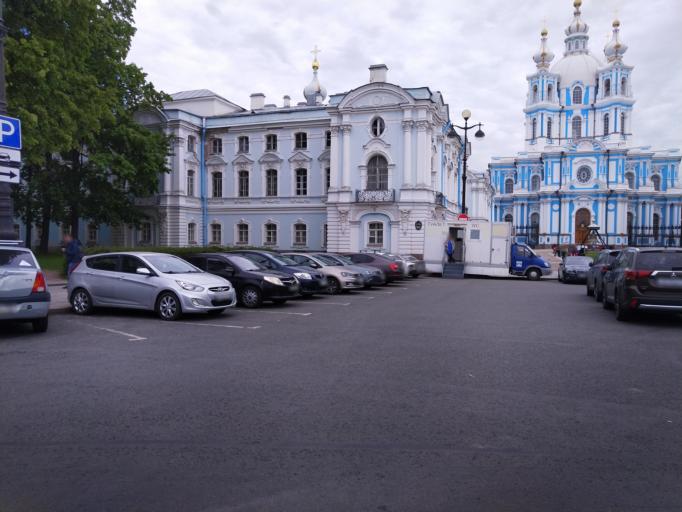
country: RU
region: Leningrad
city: Finlyandskiy
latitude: 59.9490
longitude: 30.3919
